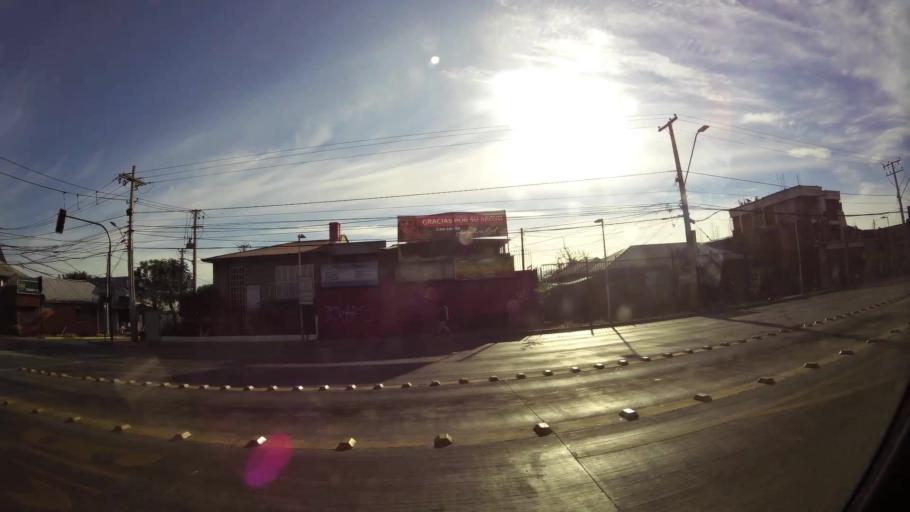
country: CL
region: Santiago Metropolitan
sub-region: Provincia de Santiago
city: Lo Prado
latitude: -33.4590
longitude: -70.7054
